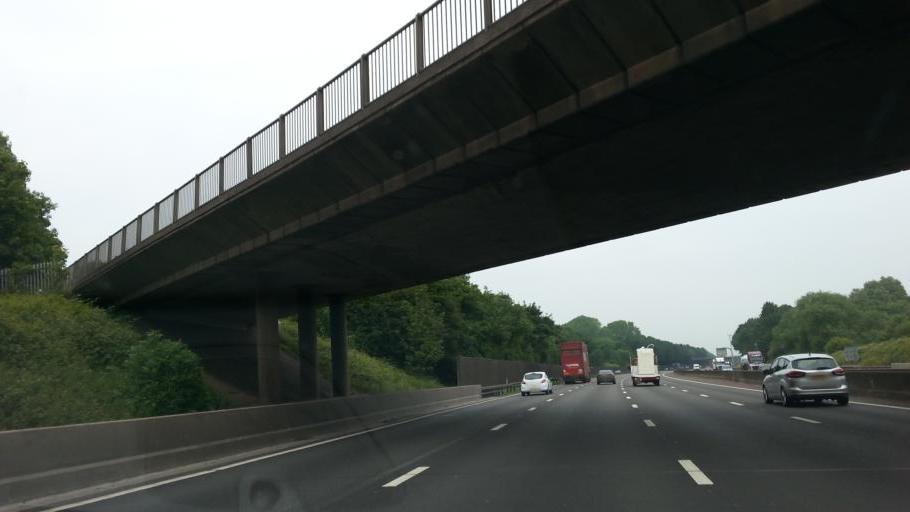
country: GB
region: England
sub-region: Staffordshire
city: Penkridge
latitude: 52.7176
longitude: -2.1023
